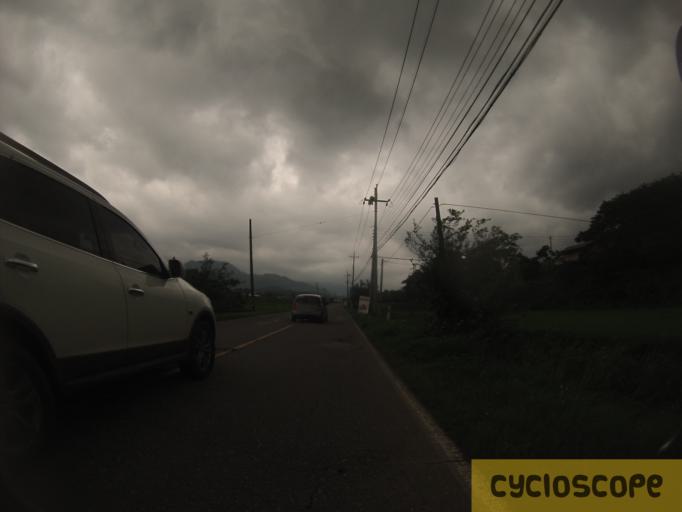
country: KR
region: Chungcheongnam-do
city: Hongsung
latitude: 36.5522
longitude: 126.7759
